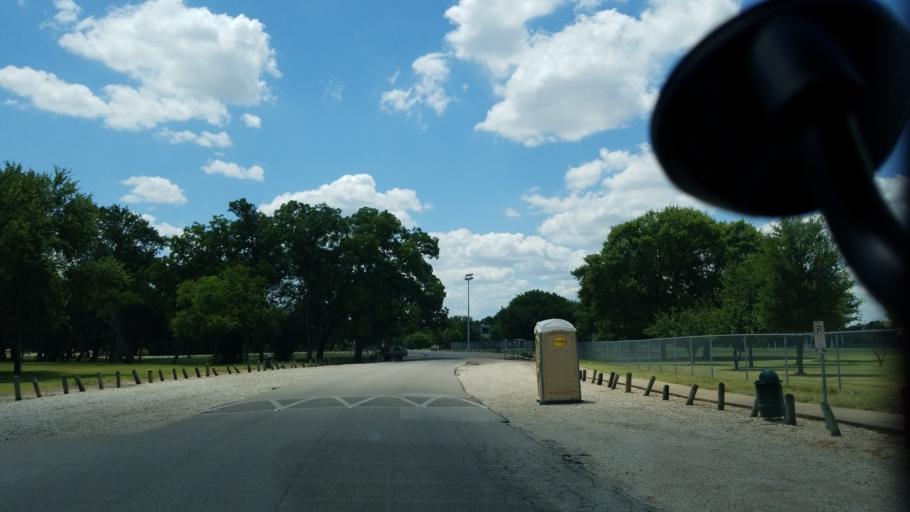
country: US
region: Texas
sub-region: Dallas County
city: Cockrell Hill
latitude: 32.7113
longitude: -96.8505
